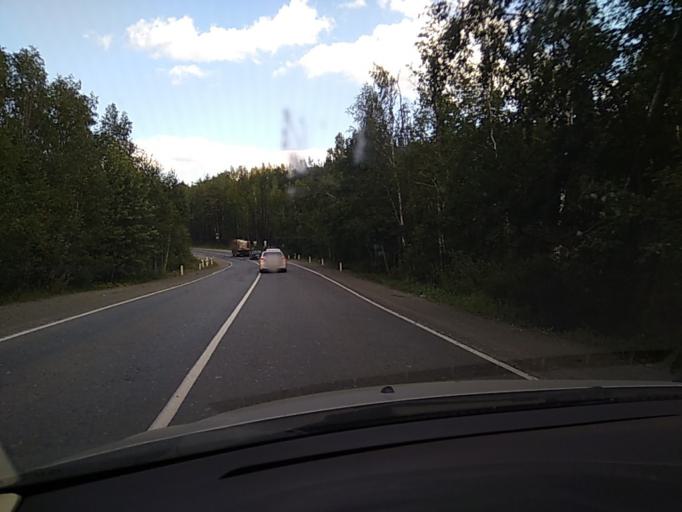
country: RU
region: Chelyabinsk
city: Karabash
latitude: 55.5008
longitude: 60.2798
